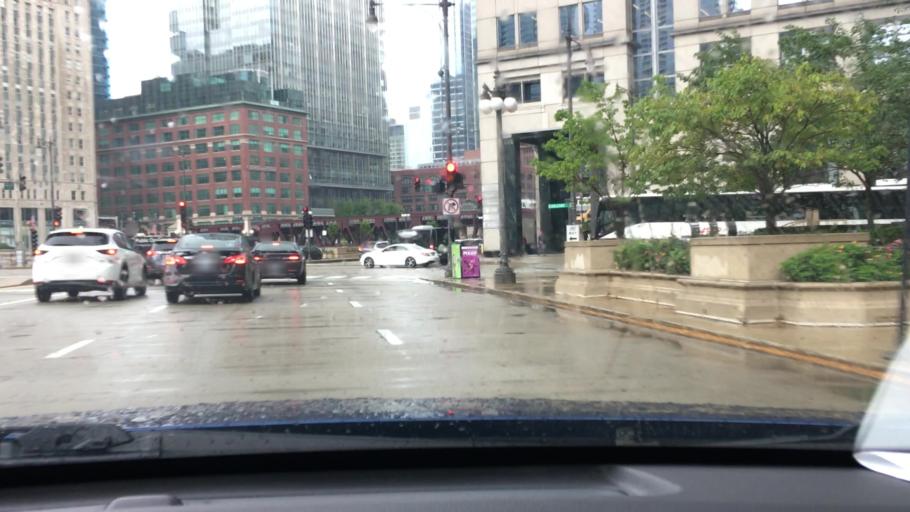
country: US
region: Illinois
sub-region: Cook County
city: Chicago
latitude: 41.8864
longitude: -87.6360
